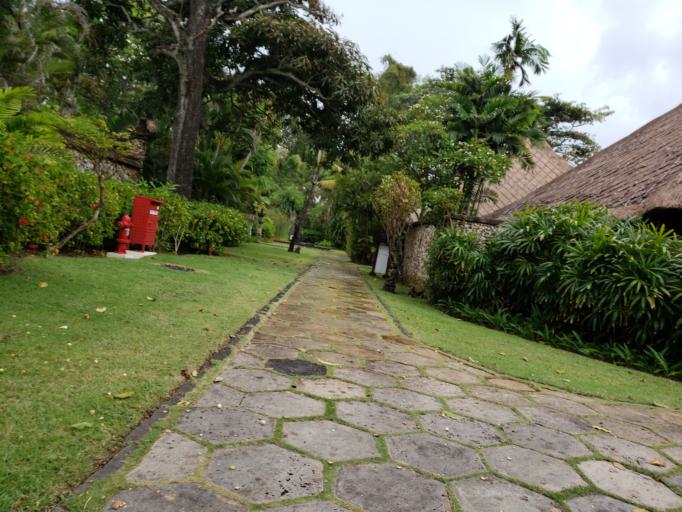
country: ID
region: Bali
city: Kuta
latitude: -8.6899
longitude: 115.1574
